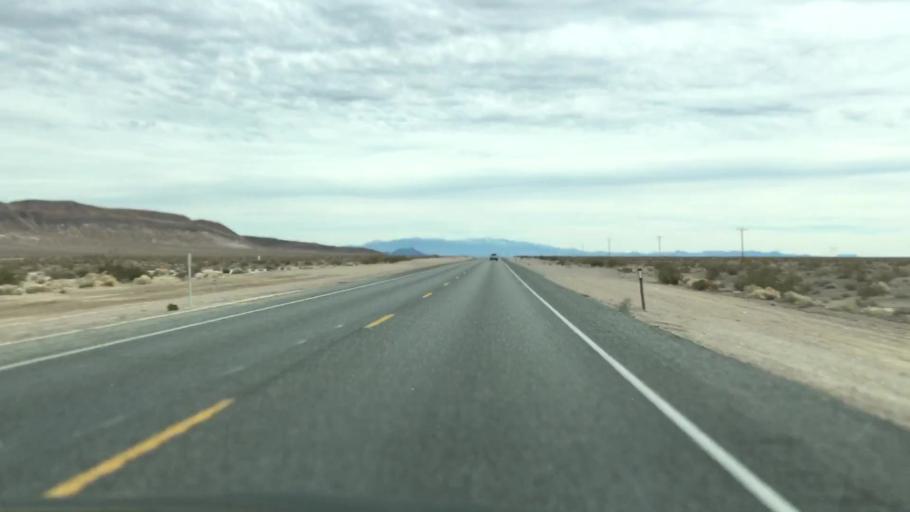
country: US
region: Nevada
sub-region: Nye County
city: Beatty
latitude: 36.6946
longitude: -116.5715
